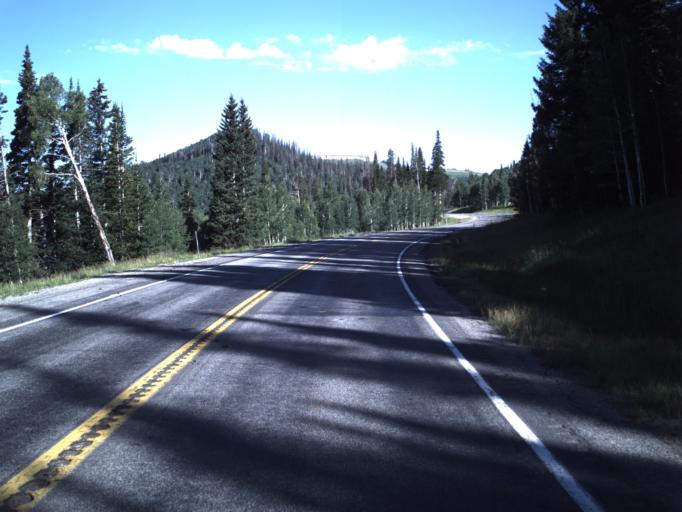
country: US
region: Utah
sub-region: Sanpete County
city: Fairview
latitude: 39.5928
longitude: -111.2660
